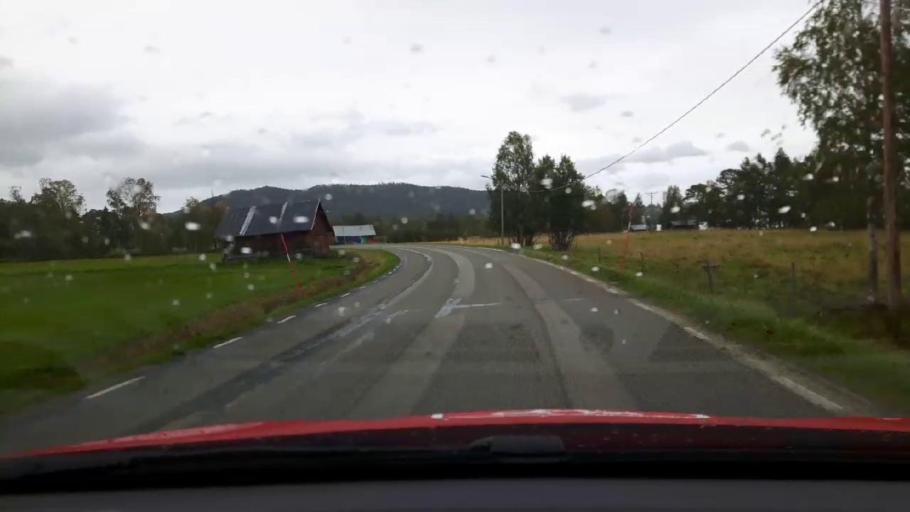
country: SE
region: Jaemtland
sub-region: Bergs Kommun
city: Hoverberg
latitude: 62.7973
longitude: 14.4392
